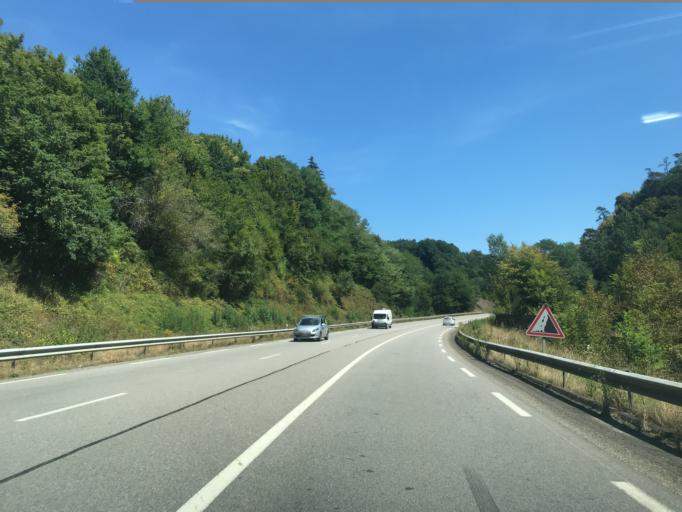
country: FR
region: Limousin
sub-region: Departement de la Correze
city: Laguenne
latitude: 45.2567
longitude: 1.7783
